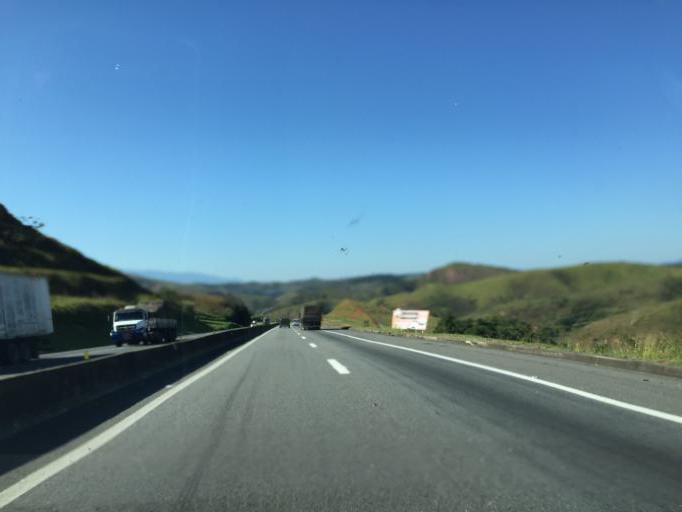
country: BR
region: Sao Paulo
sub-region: Cruzeiro
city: Cruzeiro
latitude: -22.6341
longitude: -44.9322
